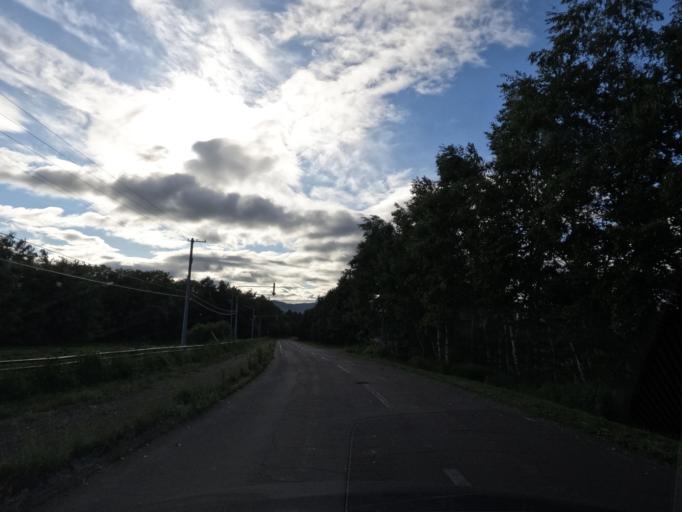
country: JP
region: Hokkaido
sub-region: Asahikawa-shi
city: Asahikawa
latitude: 43.6272
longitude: 142.4445
